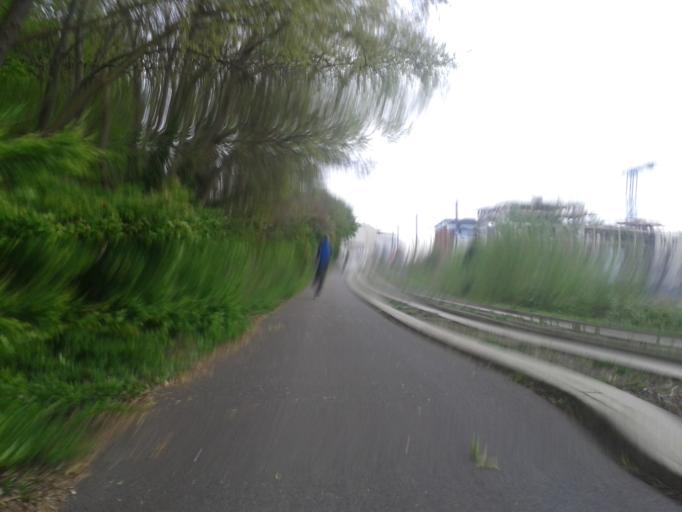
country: GB
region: England
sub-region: Cambridgeshire
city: Cambridge
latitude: 52.1850
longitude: 0.1312
